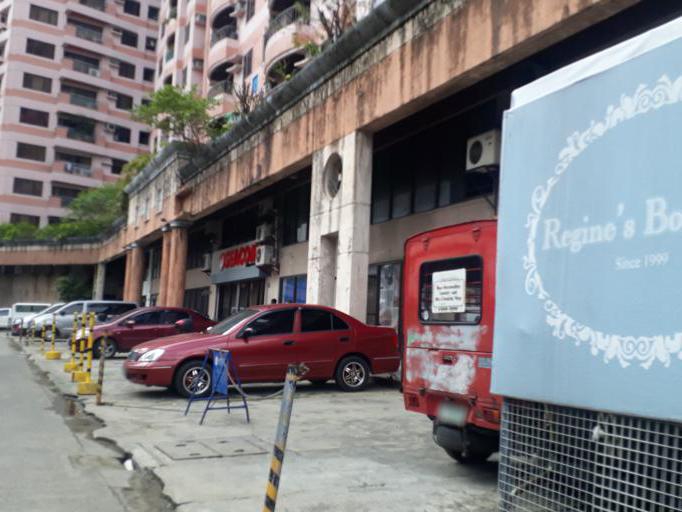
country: PH
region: Metro Manila
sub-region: San Juan
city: San Juan
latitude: 14.6106
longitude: 121.0337
